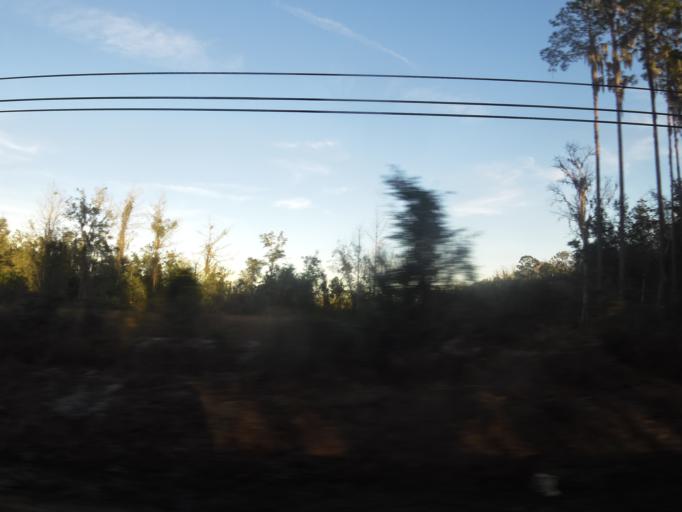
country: US
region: Florida
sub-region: Putnam County
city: East Palatka
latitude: 29.8256
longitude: -81.5533
